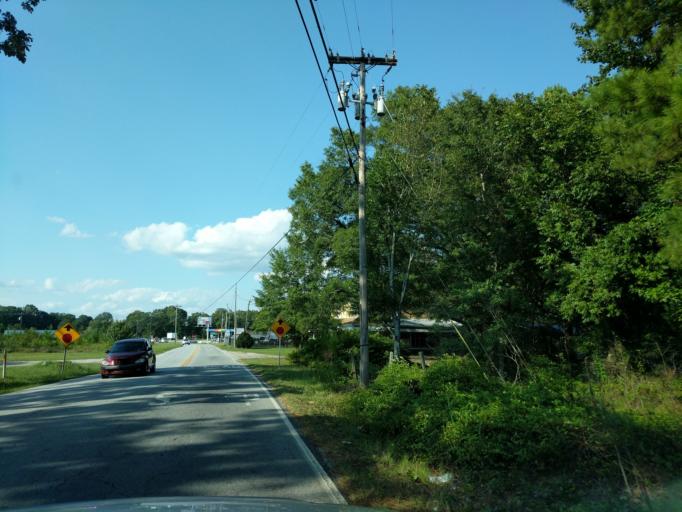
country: US
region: South Carolina
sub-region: Greenville County
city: Fountain Inn
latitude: 34.6724
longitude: -82.2187
